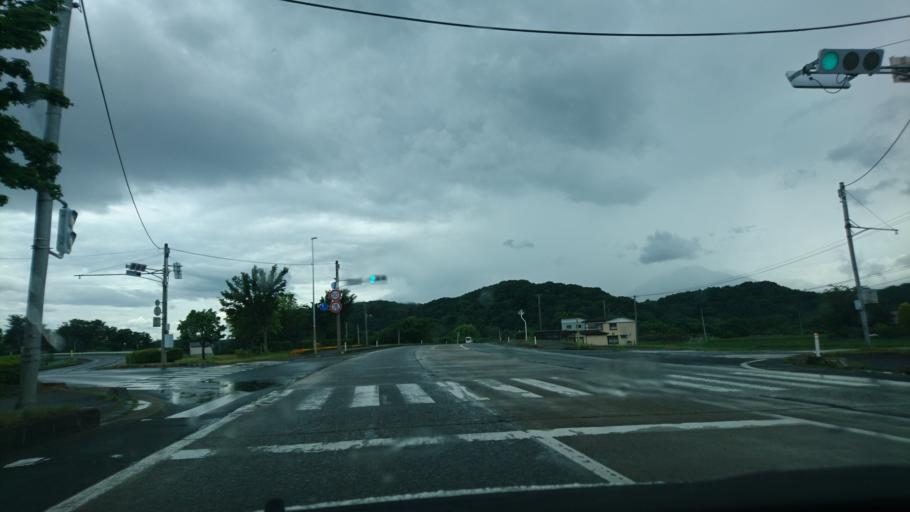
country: JP
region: Iwate
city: Morioka-shi
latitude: 39.9313
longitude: 141.1999
